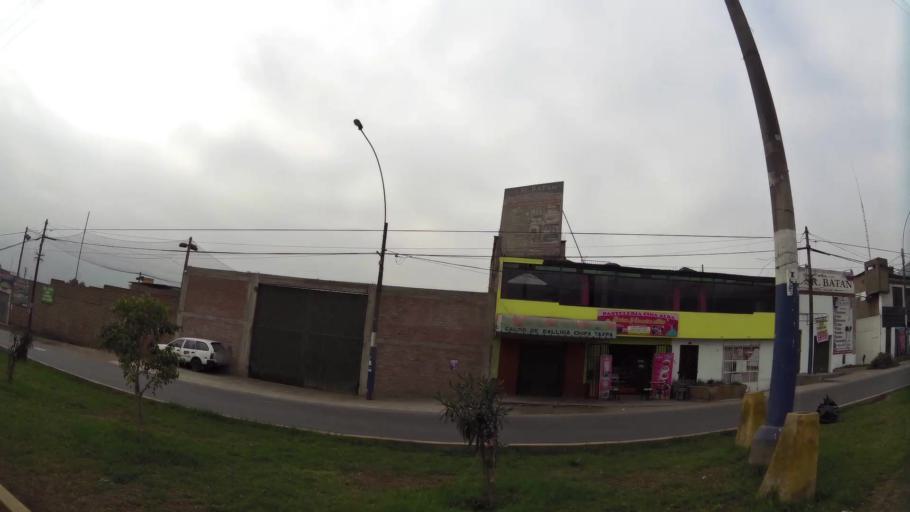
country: PE
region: Lima
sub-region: Lima
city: Independencia
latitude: -11.9787
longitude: -76.9909
